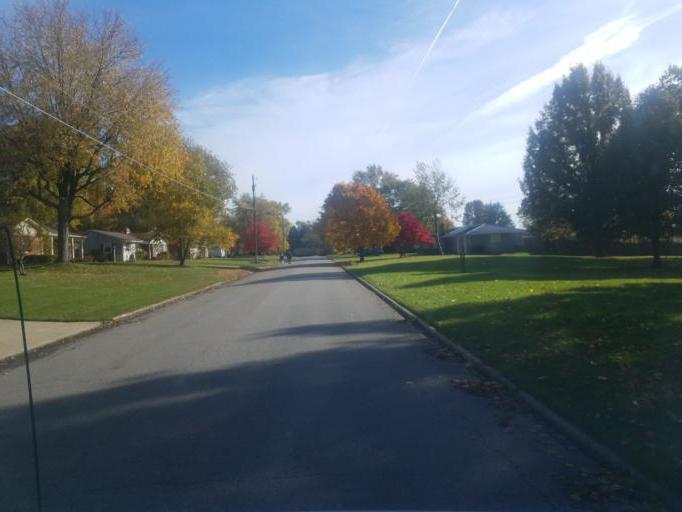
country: US
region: Ohio
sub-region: Richland County
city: Mansfield
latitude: 40.7272
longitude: -82.5167
